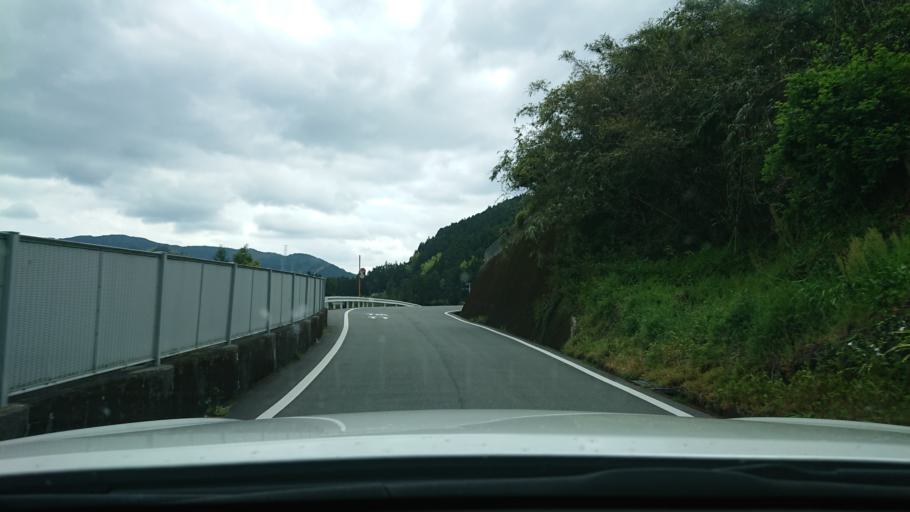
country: JP
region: Tokushima
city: Ishii
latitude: 33.9251
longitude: 134.4226
